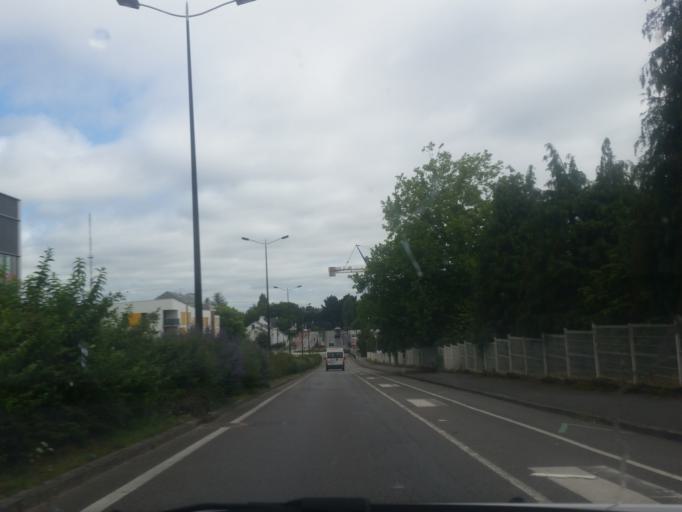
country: FR
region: Pays de la Loire
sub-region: Departement de la Loire-Atlantique
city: Nantes
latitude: 47.2503
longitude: -1.5540
